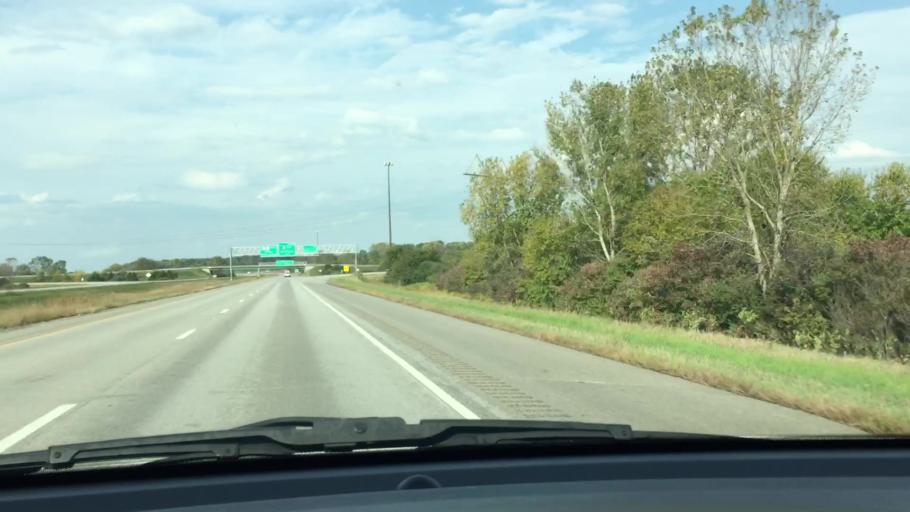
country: US
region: Illinois
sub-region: Henry County
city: Colona
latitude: 41.5350
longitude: -90.3200
